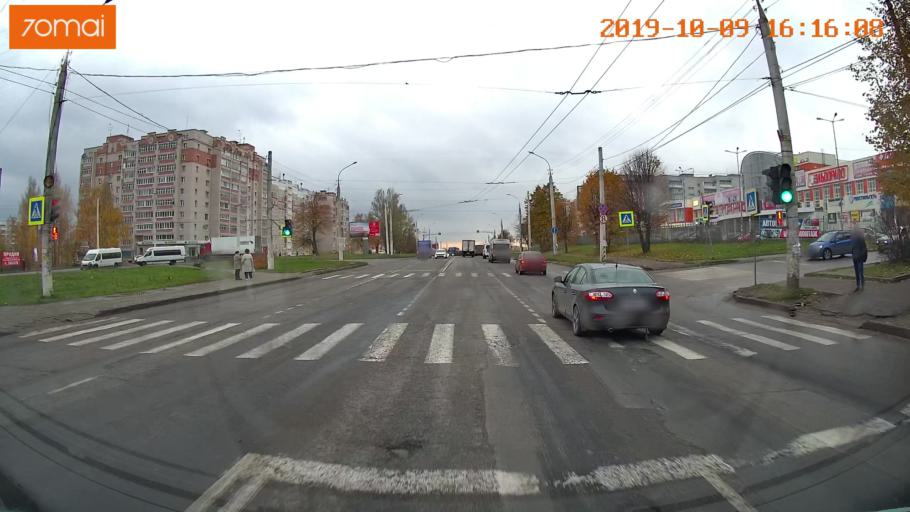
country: RU
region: Kostroma
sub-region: Kostromskoy Rayon
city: Kostroma
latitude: 57.7363
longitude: 40.9108
